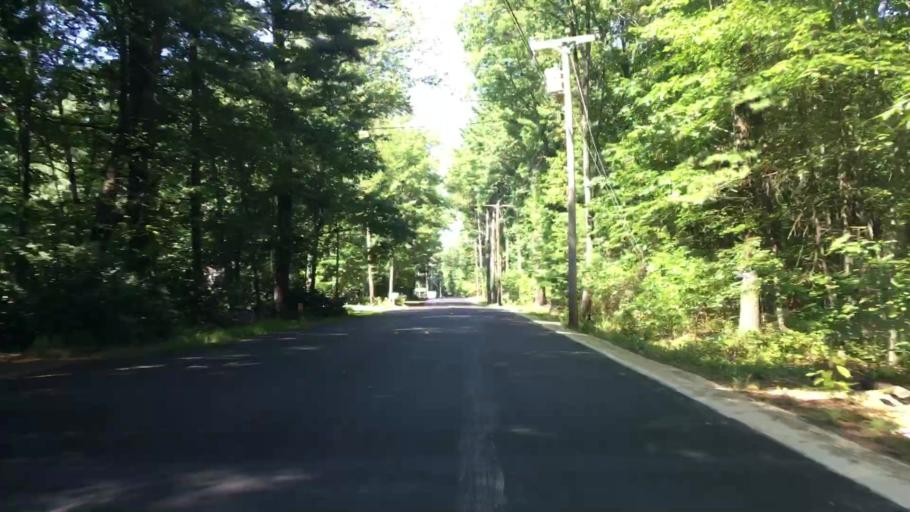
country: US
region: Maine
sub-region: York County
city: Eliot
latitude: 43.1622
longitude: -70.8396
